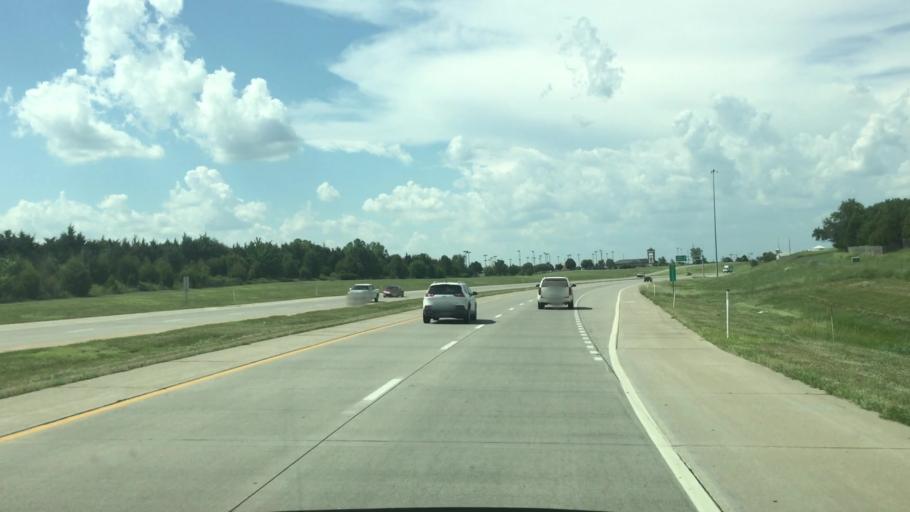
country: US
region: Kansas
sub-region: Butler County
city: Andover
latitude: 37.7022
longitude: -97.1982
